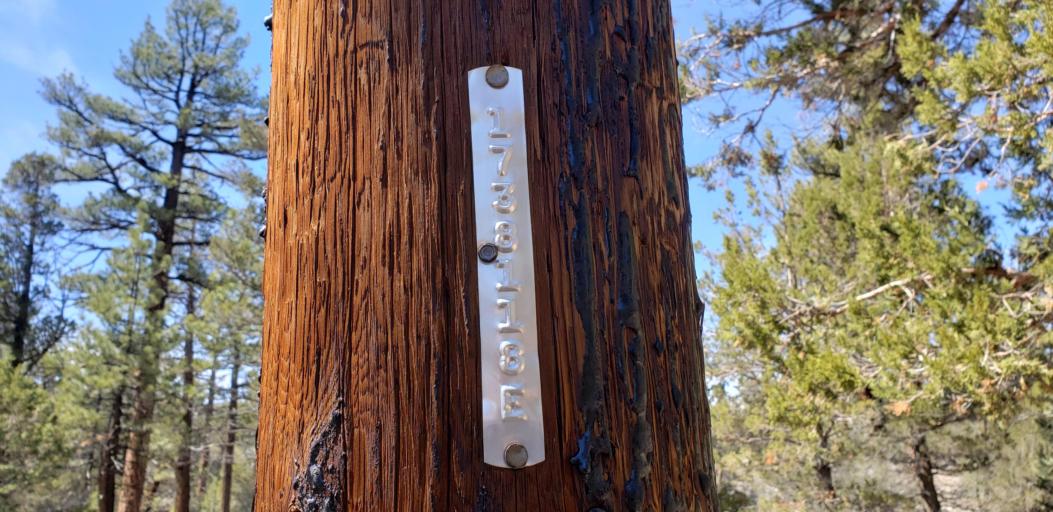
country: US
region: California
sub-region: San Bernardino County
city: Big Bear Lake
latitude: 34.3133
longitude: -116.9284
